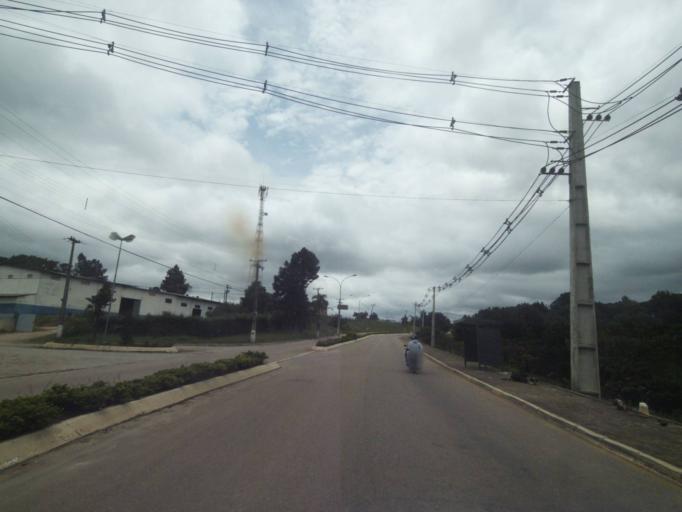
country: BR
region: Parana
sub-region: Campina Grande Do Sul
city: Campina Grande do Sul
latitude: -25.3088
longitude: -49.0605
